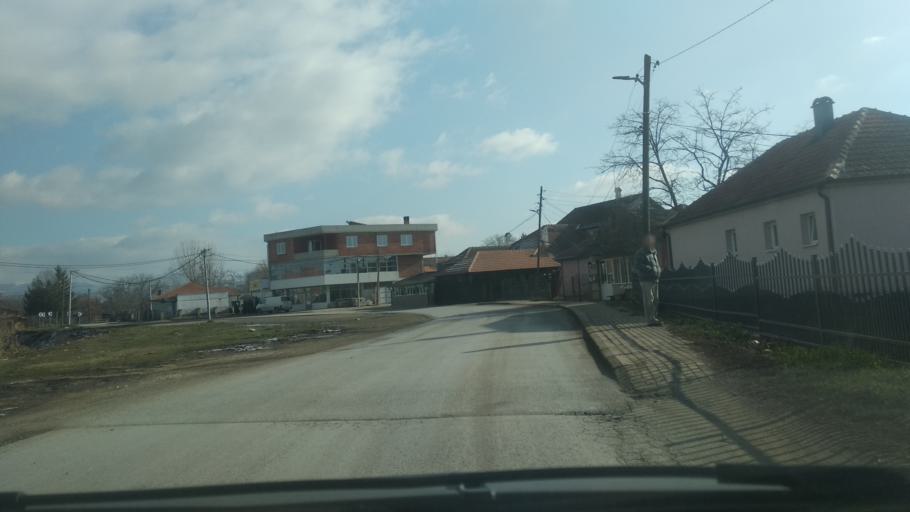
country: XK
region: Pristina
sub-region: Lipjan
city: Lipljan
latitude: 42.5940
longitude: 21.1399
